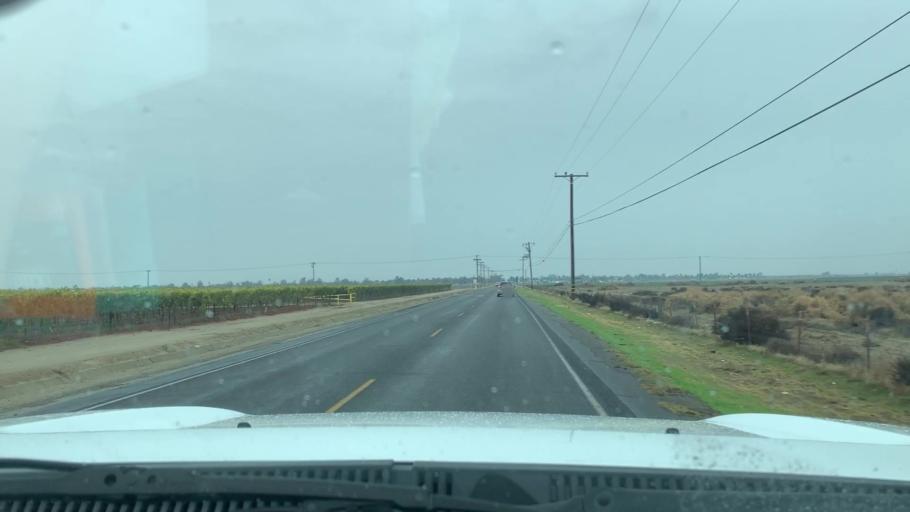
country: US
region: California
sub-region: Kern County
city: Delano
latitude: 35.7613
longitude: -119.2794
